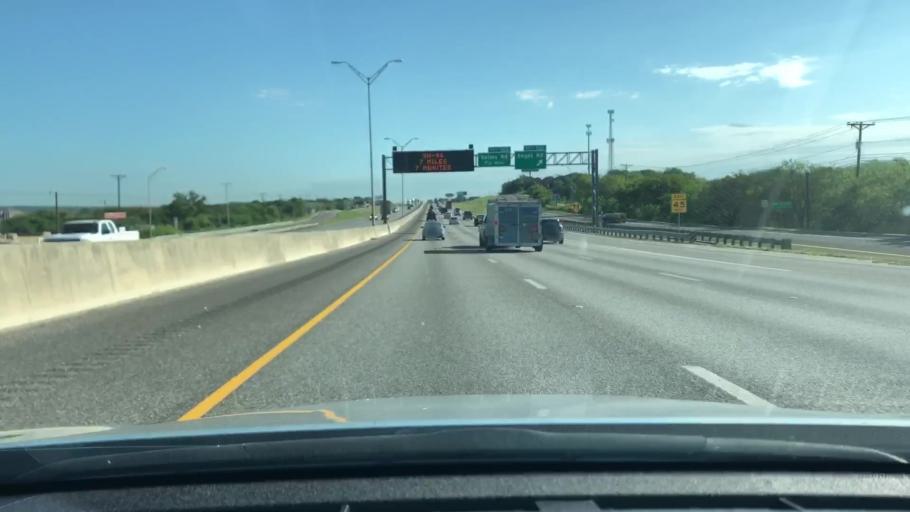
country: US
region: Texas
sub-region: Guadalupe County
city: Northcliff
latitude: 29.6496
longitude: -98.1954
